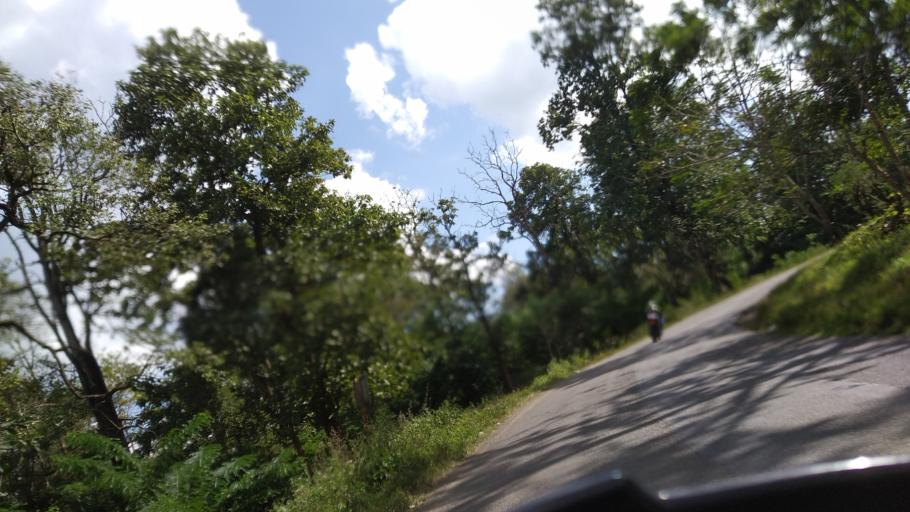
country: IN
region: Kerala
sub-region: Wayanad
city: Panamaram
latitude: 11.9316
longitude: 76.0671
